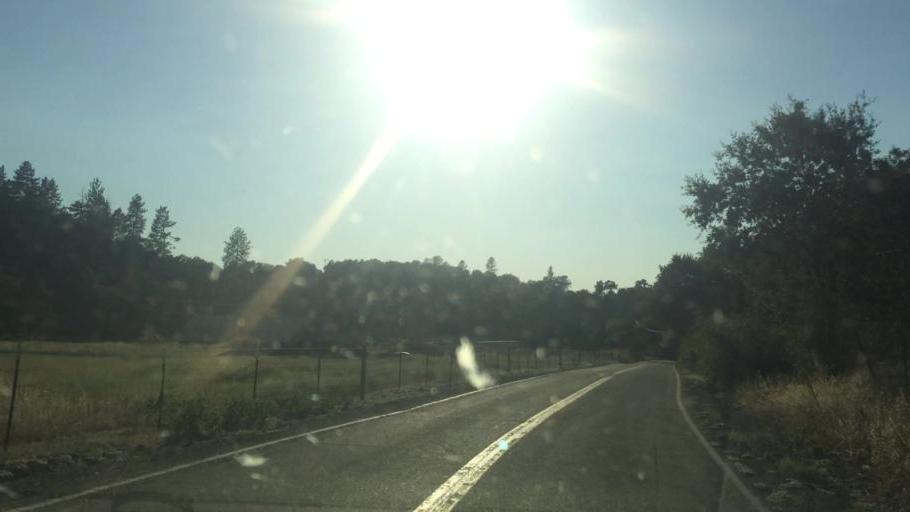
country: US
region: California
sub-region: Amador County
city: Plymouth
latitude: 38.4827
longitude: -120.8759
